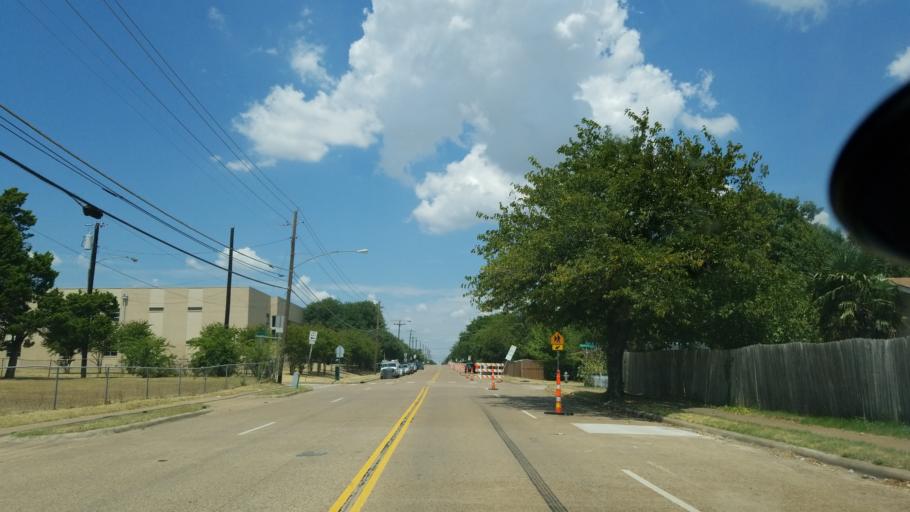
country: US
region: Texas
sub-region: Dallas County
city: Cockrell Hill
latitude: 32.7143
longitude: -96.9001
